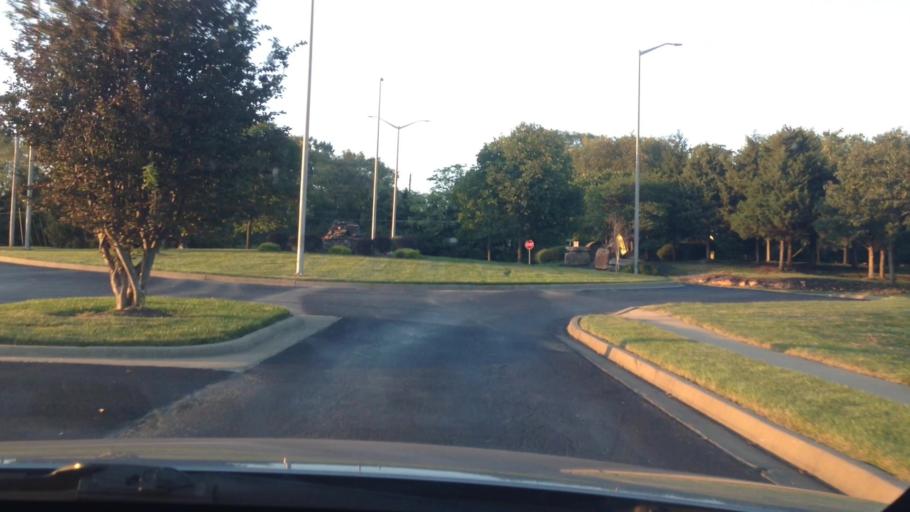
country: US
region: Missouri
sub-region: Jackson County
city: Grandview
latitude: 38.9240
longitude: -94.5592
